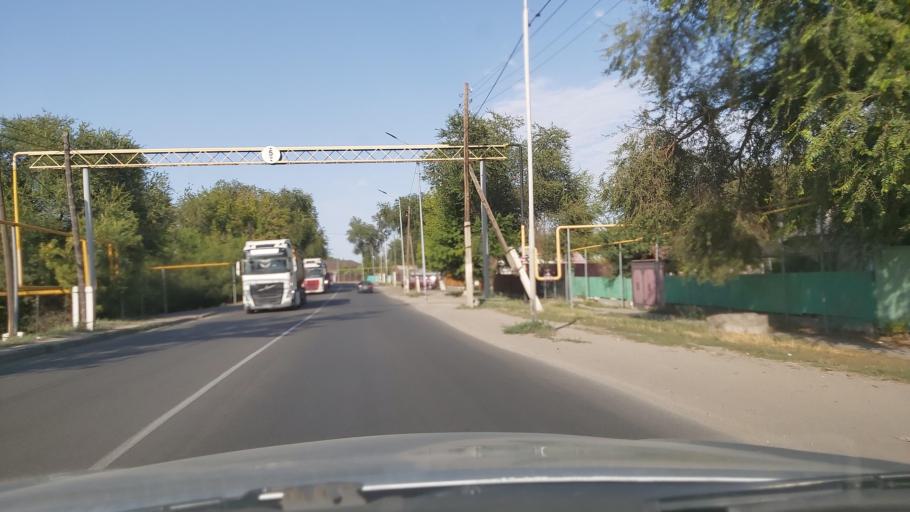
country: KZ
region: Almaty Oblysy
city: Energeticheskiy
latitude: 43.4947
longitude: 77.0383
